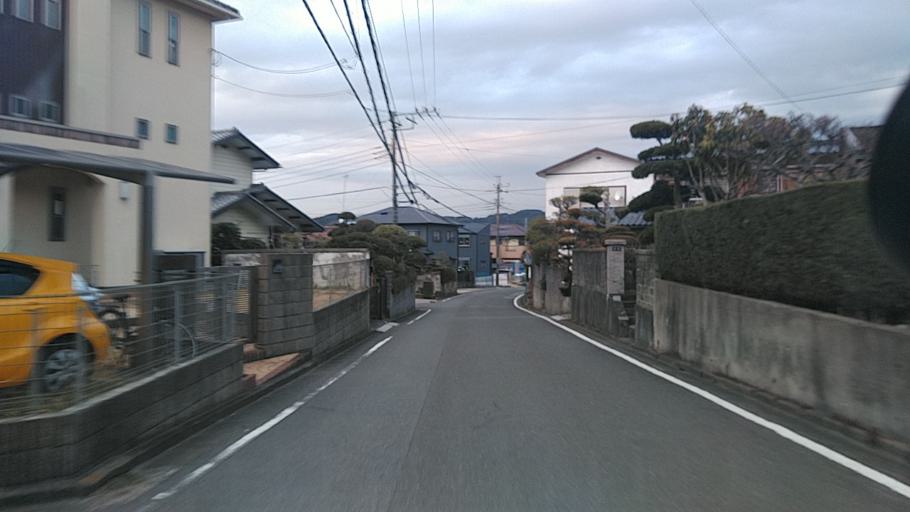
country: JP
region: Chiba
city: Kimitsu
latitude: 35.3014
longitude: 139.9579
